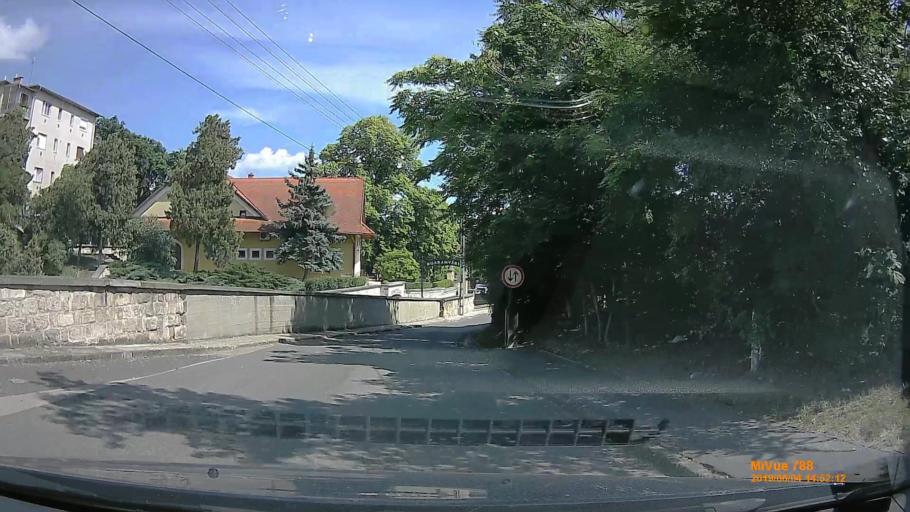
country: HU
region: Budapest
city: Budapest XXII. keruelet
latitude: 47.4186
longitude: 19.0374
